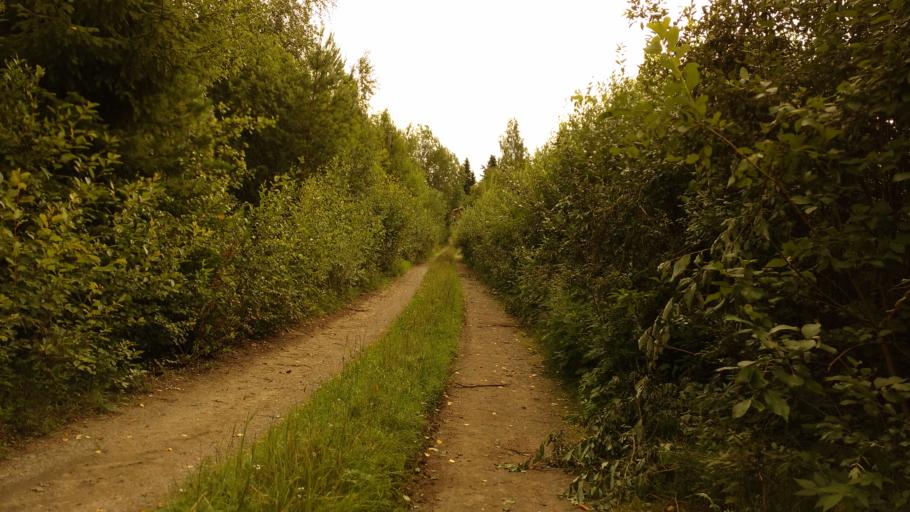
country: FI
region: Varsinais-Suomi
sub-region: Turku
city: Paimio
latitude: 60.4605
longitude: 22.6287
